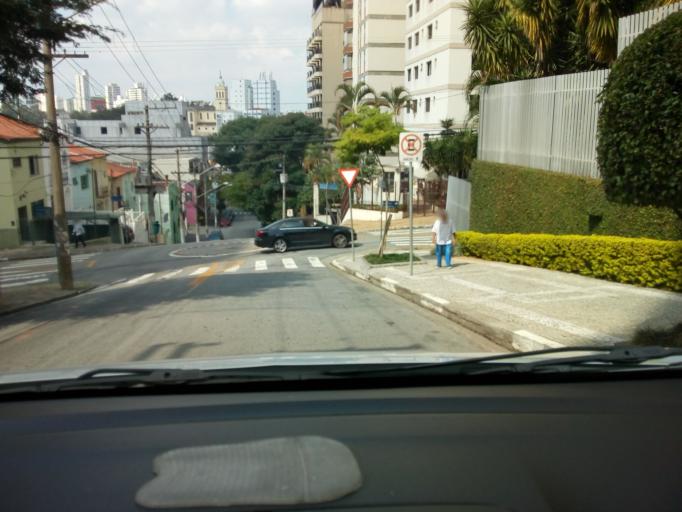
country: BR
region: Sao Paulo
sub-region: Sao Paulo
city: Sao Paulo
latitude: -23.5719
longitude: -46.6343
